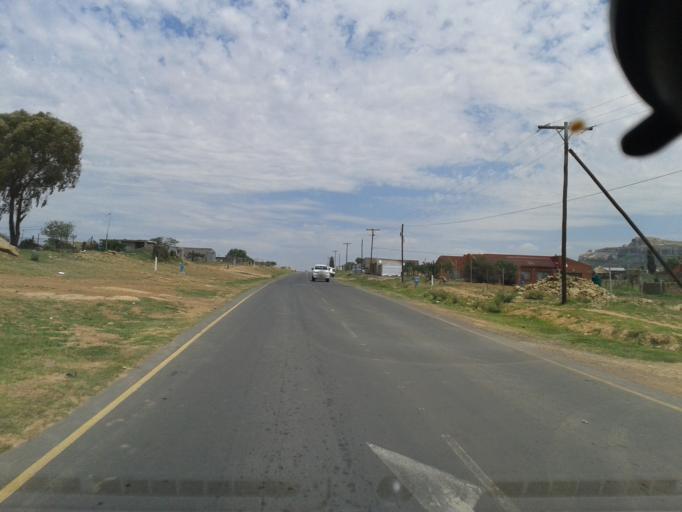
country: LS
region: Maseru
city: Maseru
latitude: -29.3558
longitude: 27.5908
